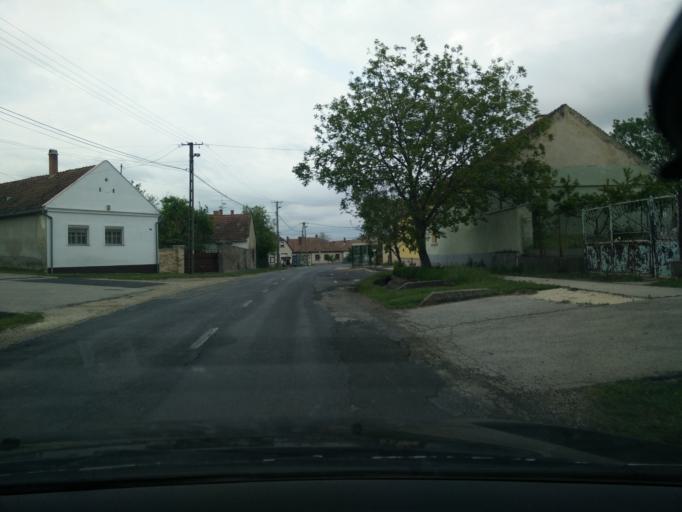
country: HU
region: Veszprem
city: Papa
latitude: 47.2846
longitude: 17.4206
